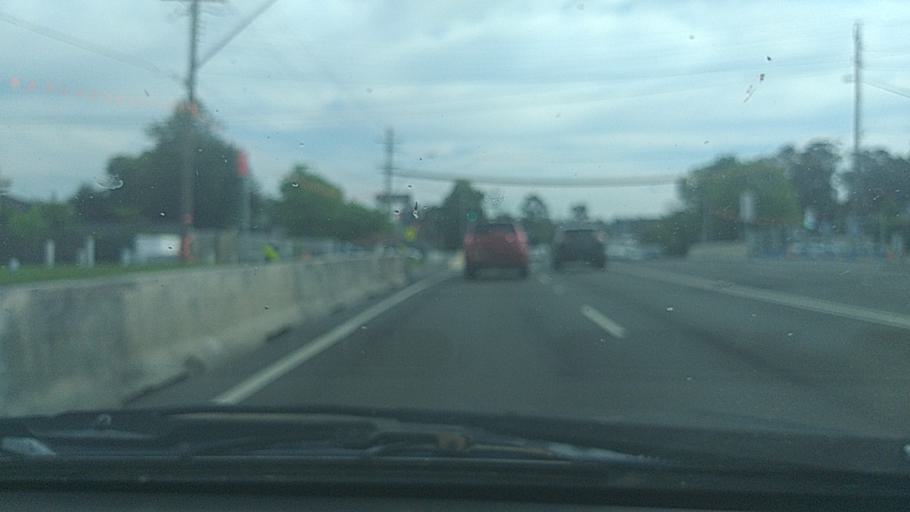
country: AU
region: New South Wales
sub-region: Penrith Municipality
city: Kingswood Park
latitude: -33.7650
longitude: 150.7097
